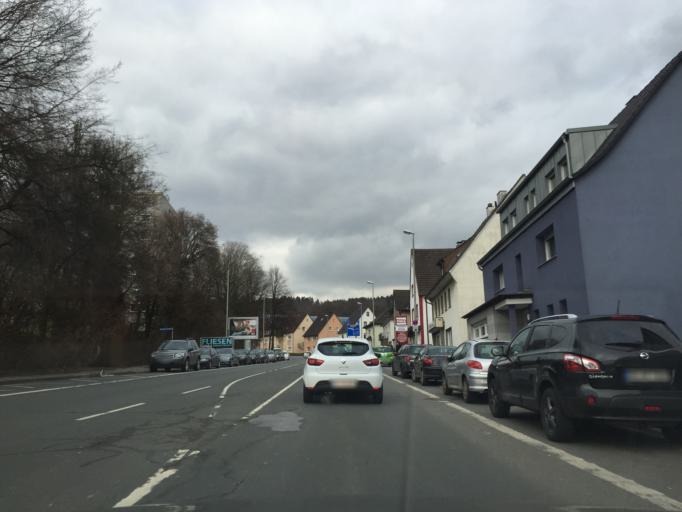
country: DE
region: North Rhine-Westphalia
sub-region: Regierungsbezirk Arnsberg
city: Nachrodt-Wiblingwerde
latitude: 51.3699
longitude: 7.6116
